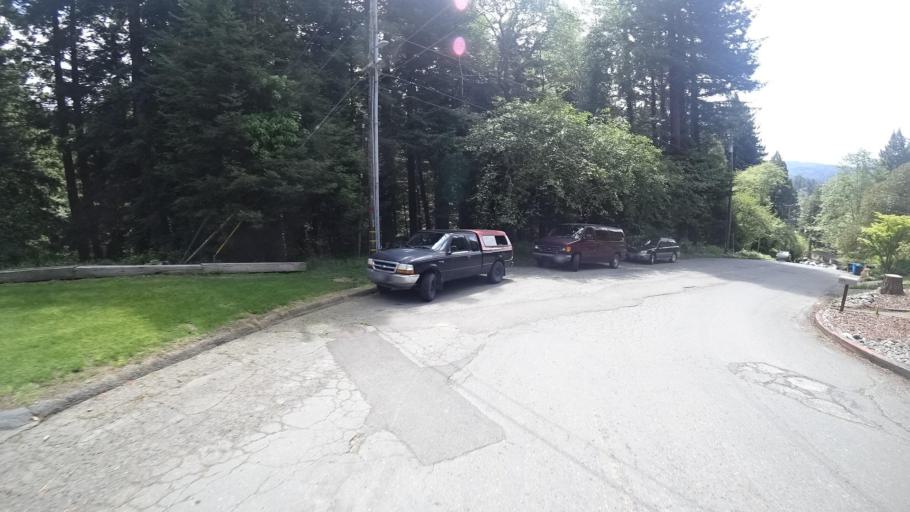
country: US
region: California
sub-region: Humboldt County
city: Arcata
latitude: 40.8631
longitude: -124.0686
